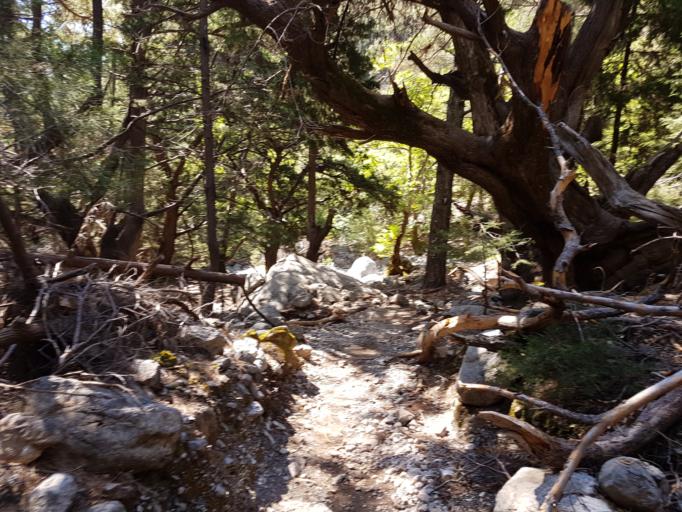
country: GR
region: Crete
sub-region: Nomos Chanias
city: Perivolia
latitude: 35.3060
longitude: 23.9369
